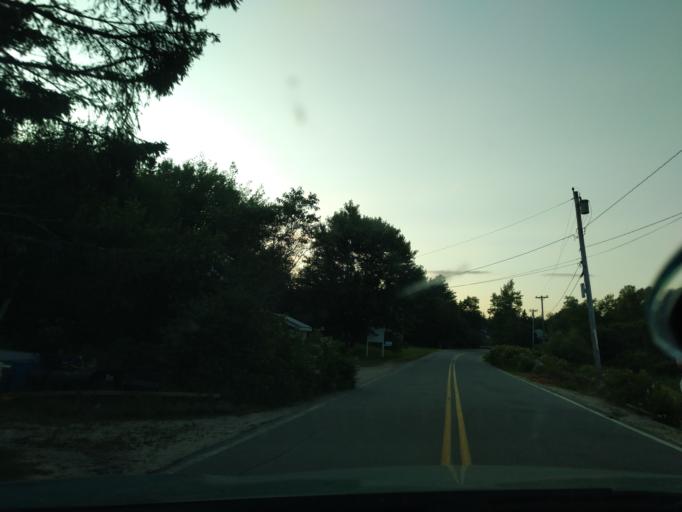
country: US
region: Maine
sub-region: Hancock County
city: Gouldsboro
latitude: 44.3654
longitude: -68.0387
